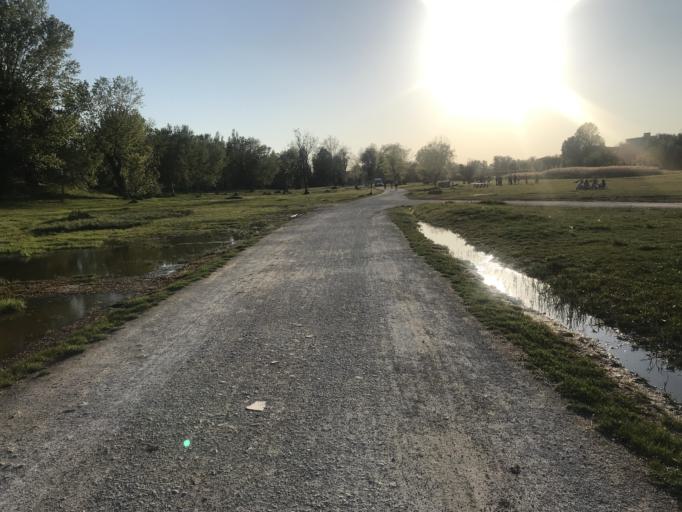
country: IT
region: Emilia-Romagna
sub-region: Provincia di Rimini
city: Rimini
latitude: 44.0631
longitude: 12.5620
